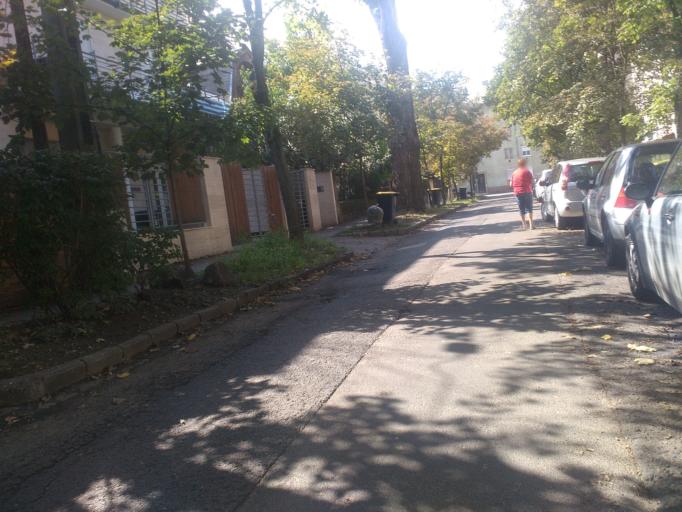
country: HU
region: Budapest
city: Budapest XI. keruelet
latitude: 47.4589
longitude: 19.0421
